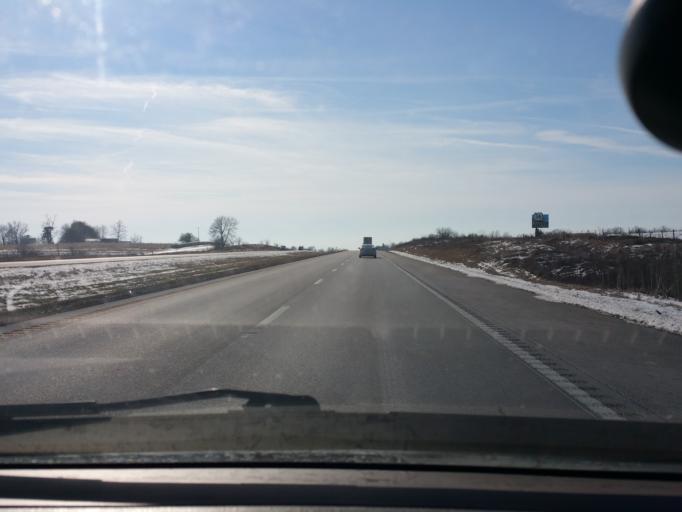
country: US
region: Missouri
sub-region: Clinton County
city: Cameron
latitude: 39.8001
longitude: -94.2007
